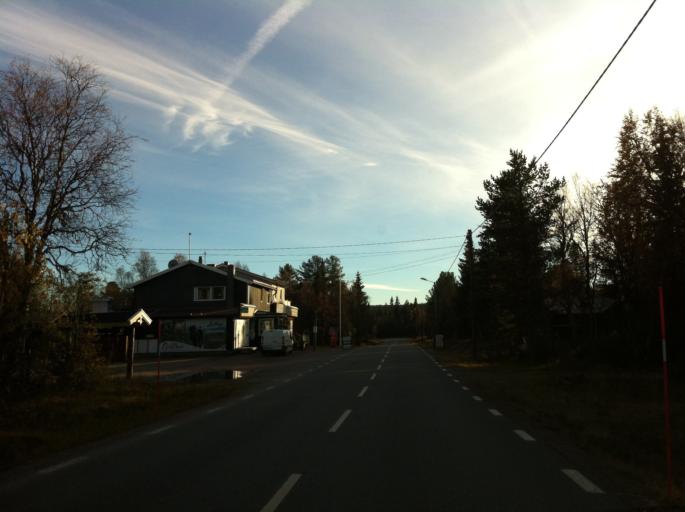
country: NO
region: Hedmark
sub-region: Engerdal
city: Engerdal
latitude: 62.0660
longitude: 12.2236
